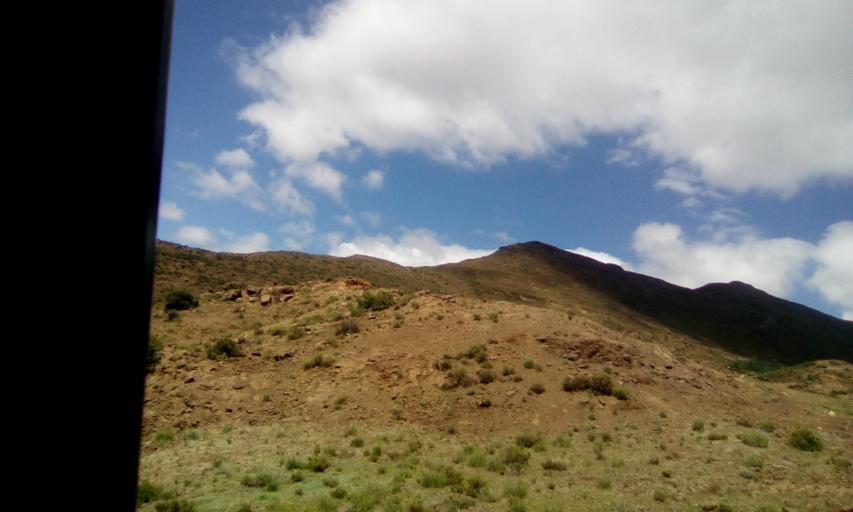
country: LS
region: Maseru
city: Nako
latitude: -29.6576
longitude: 27.7838
